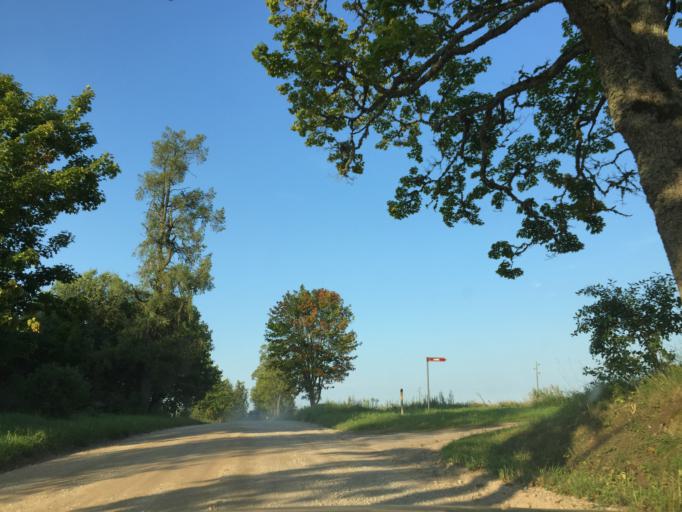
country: LV
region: Limbazu Rajons
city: Limbazi
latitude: 57.5525
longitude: 24.8002
